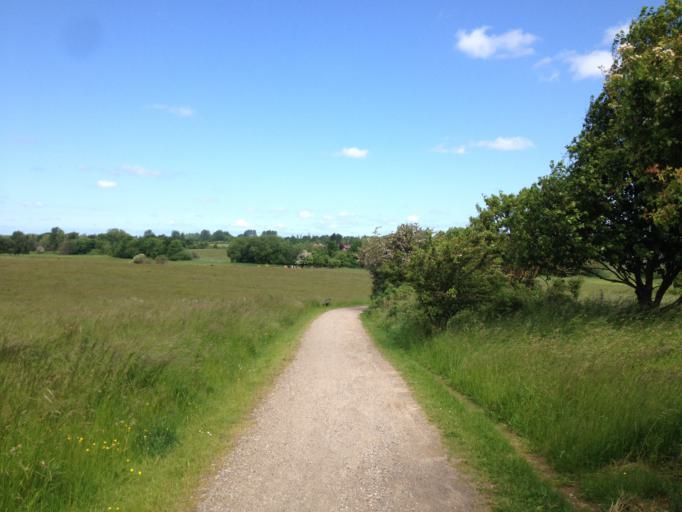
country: DK
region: Capital Region
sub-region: Fredensborg Kommune
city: Niva
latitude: 55.9267
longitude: 12.4900
